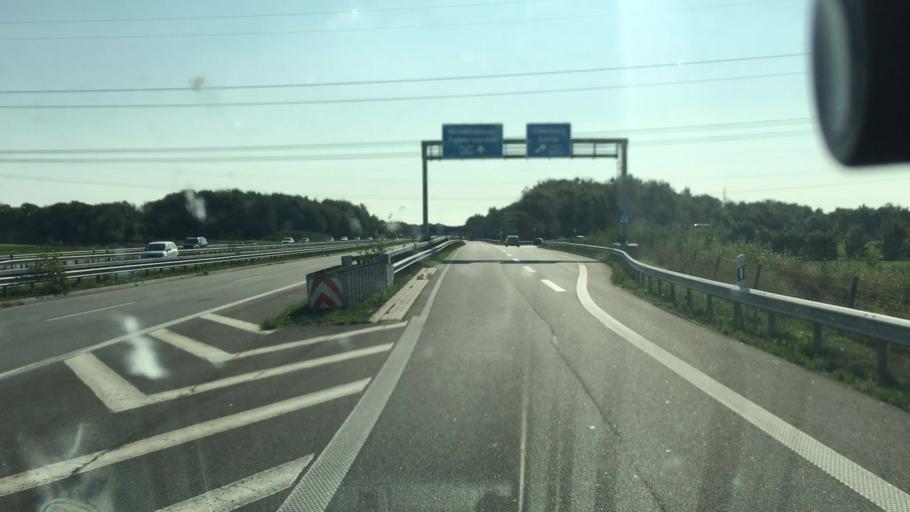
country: DE
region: Lower Saxony
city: Sande
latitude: 53.5275
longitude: 7.9992
